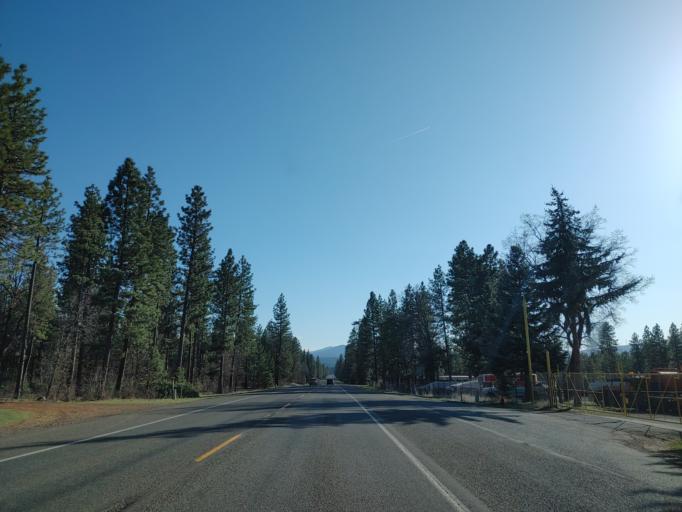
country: US
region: California
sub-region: Shasta County
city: Burney
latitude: 40.9029
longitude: -121.6409
